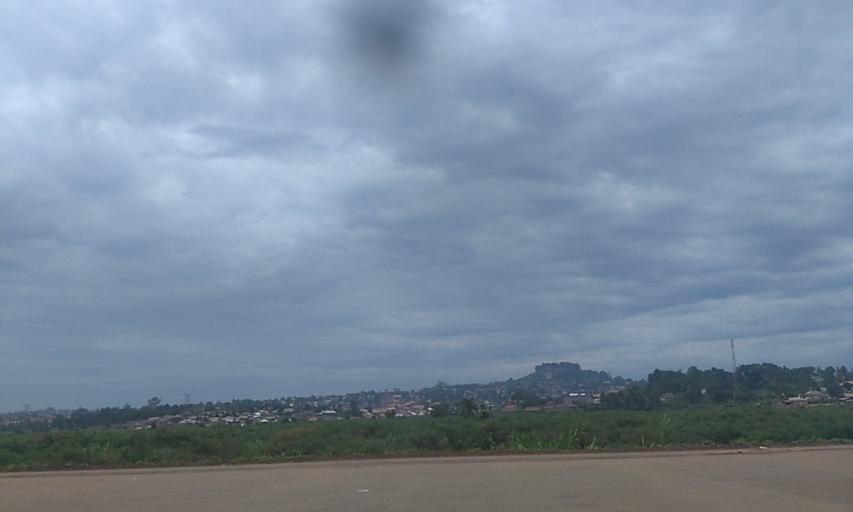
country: UG
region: Central Region
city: Kampala Central Division
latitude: 0.3269
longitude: 32.5240
